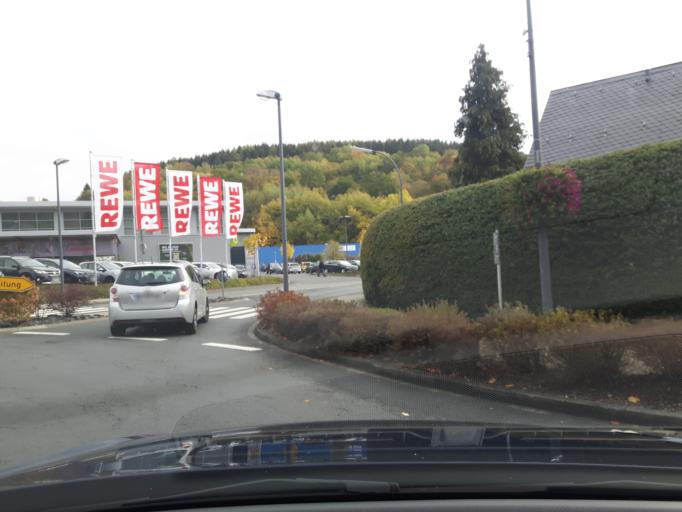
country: DE
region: North Rhine-Westphalia
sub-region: Regierungsbezirk Arnsberg
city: Bad Berleburg
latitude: 51.0561
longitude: 8.3940
